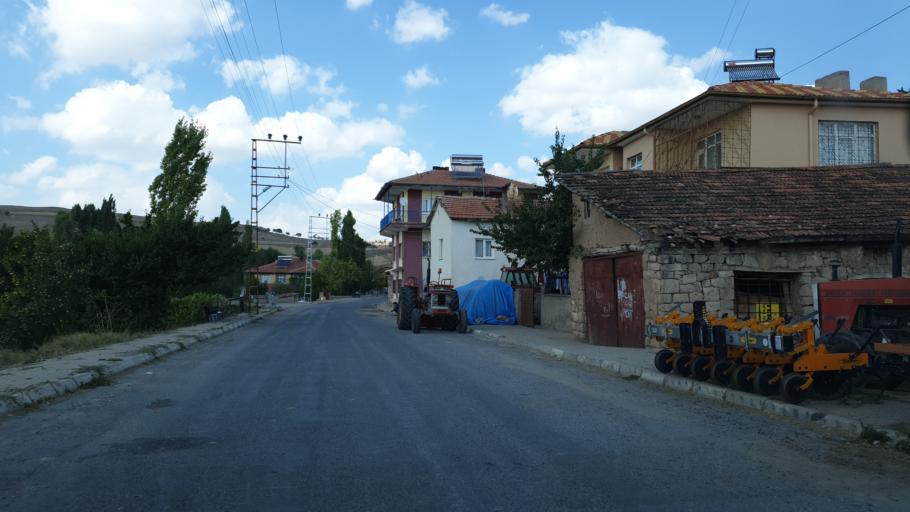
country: TR
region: Kayseri
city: Felahiye
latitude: 39.0921
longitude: 35.5631
